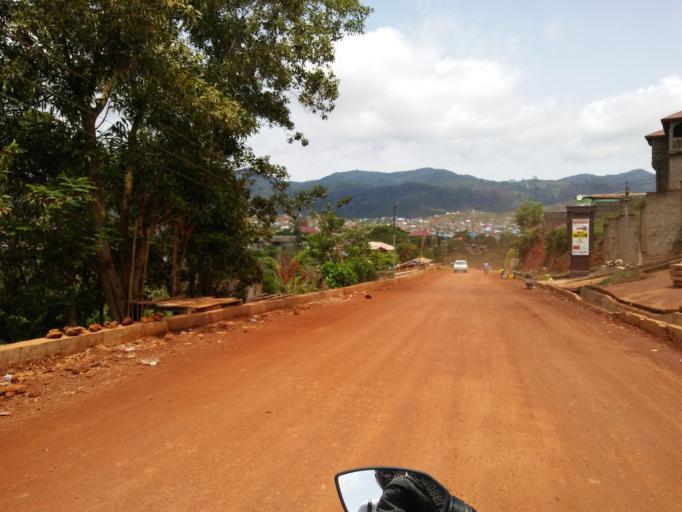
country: SL
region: Western Area
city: Hastings
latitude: 8.3990
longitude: -13.1479
